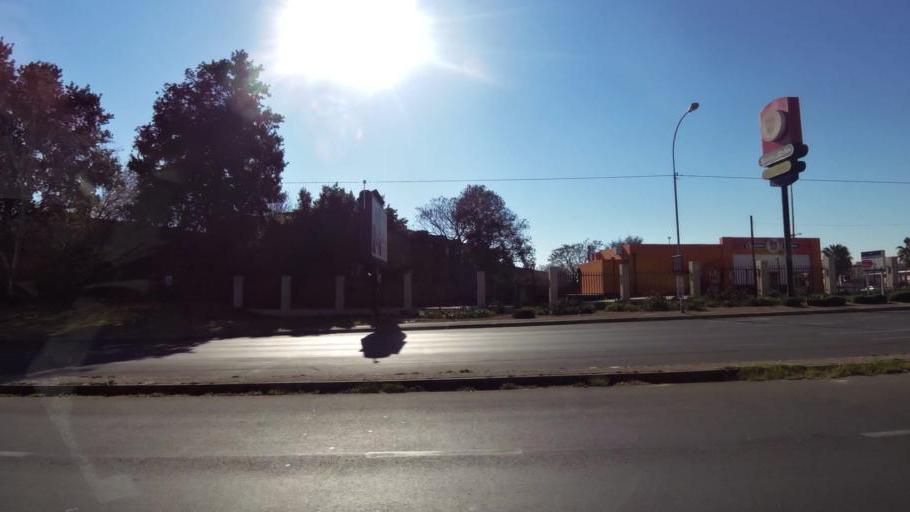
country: ZA
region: Gauteng
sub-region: City of Johannesburg Metropolitan Municipality
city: Johannesburg
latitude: -26.2412
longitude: 28.0037
